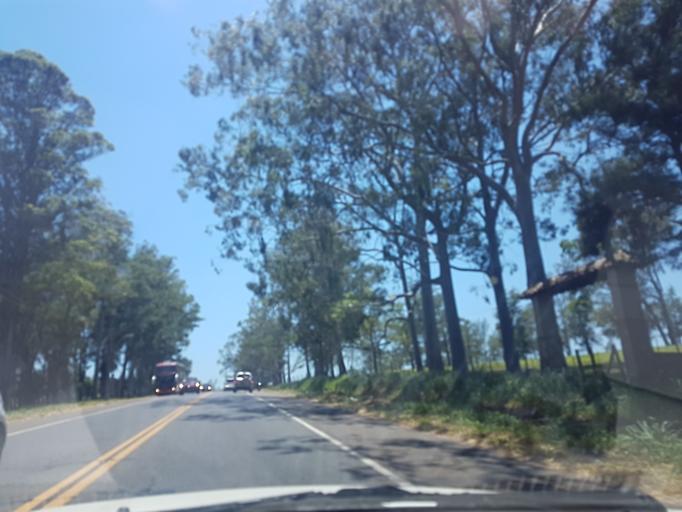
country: PY
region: Cordillera
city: Caacupe
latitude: -25.3896
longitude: -57.0656
